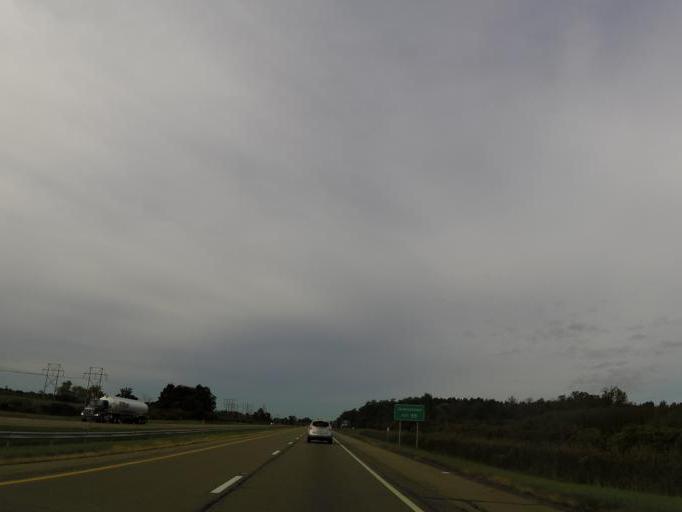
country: US
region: New York
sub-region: Chautauqua County
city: Dunkirk
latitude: 42.4704
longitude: -79.2837
